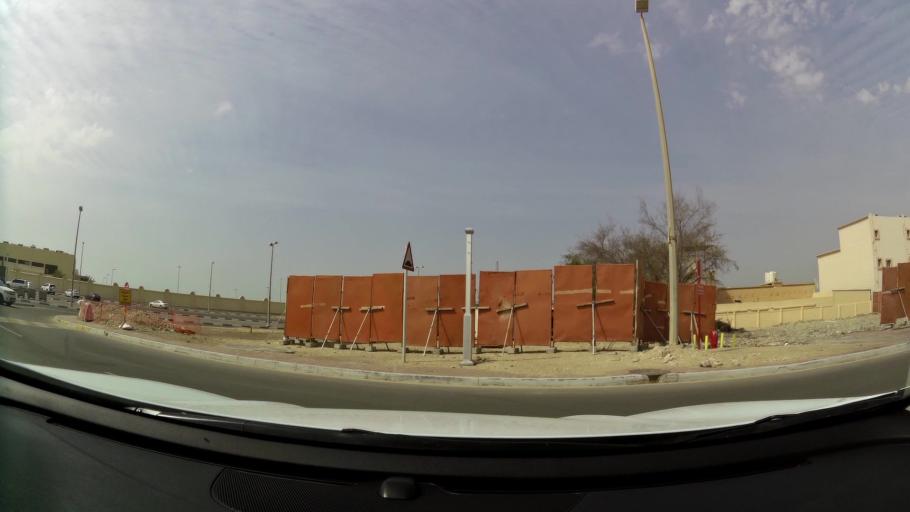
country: AE
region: Abu Dhabi
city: Abu Dhabi
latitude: 24.5576
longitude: 54.6786
